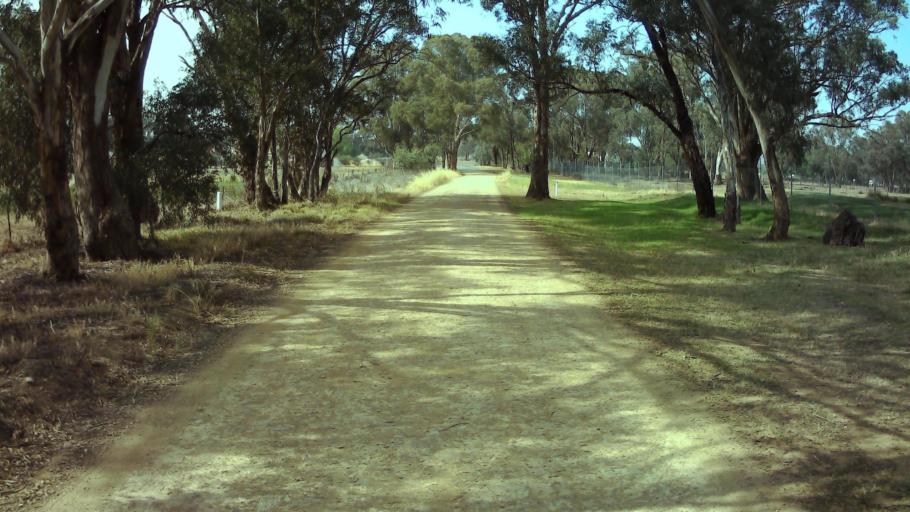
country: AU
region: New South Wales
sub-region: Weddin
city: Grenfell
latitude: -33.9034
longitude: 148.1471
